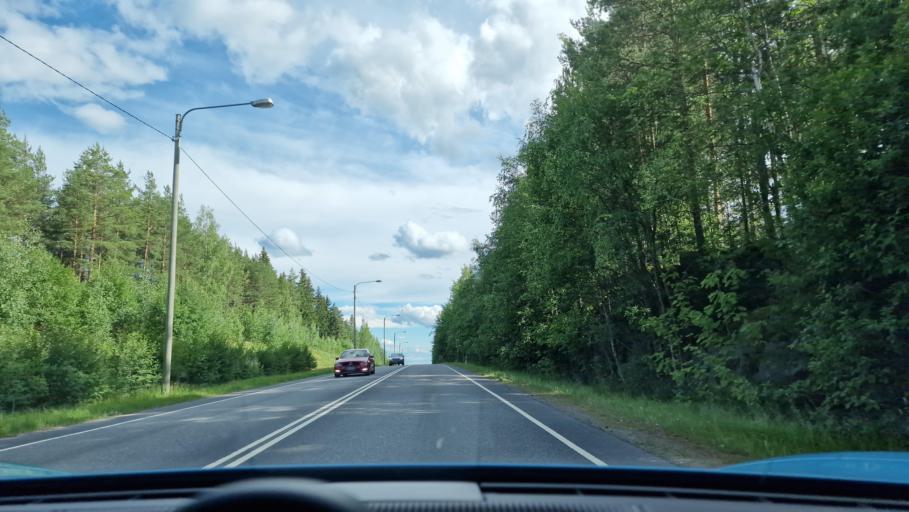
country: FI
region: Pirkanmaa
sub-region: Tampere
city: Orivesi
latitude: 61.6612
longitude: 24.3587
